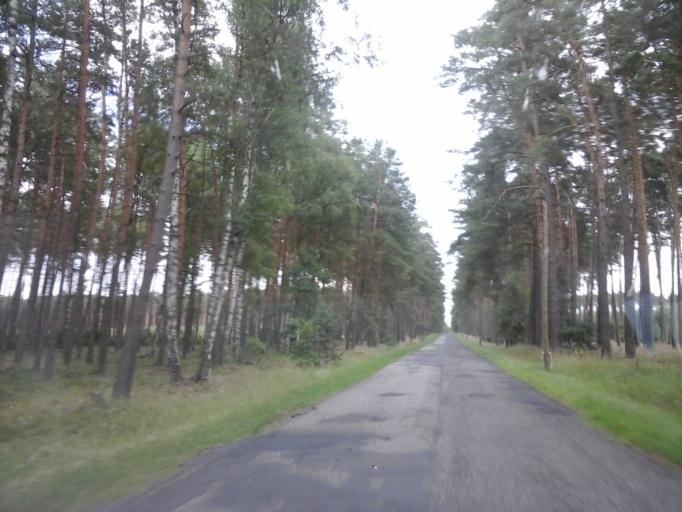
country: PL
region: West Pomeranian Voivodeship
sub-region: Powiat goleniowski
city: Goleniow
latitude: 53.4641
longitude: 14.8081
